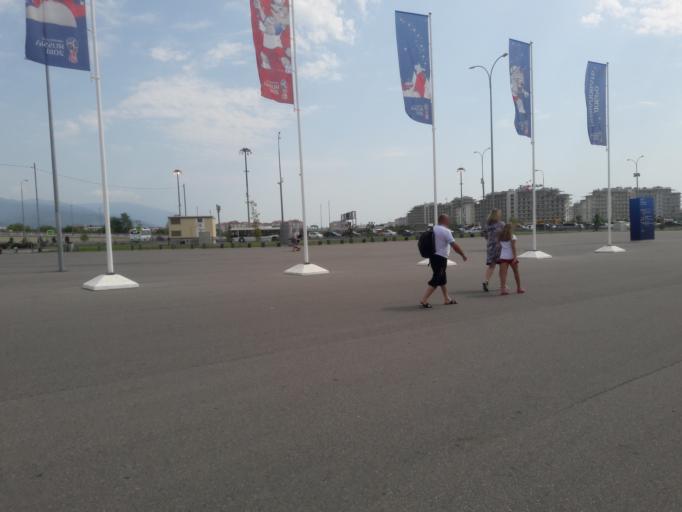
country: RU
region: Krasnodarskiy
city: Adler
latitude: 43.4086
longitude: 39.9725
